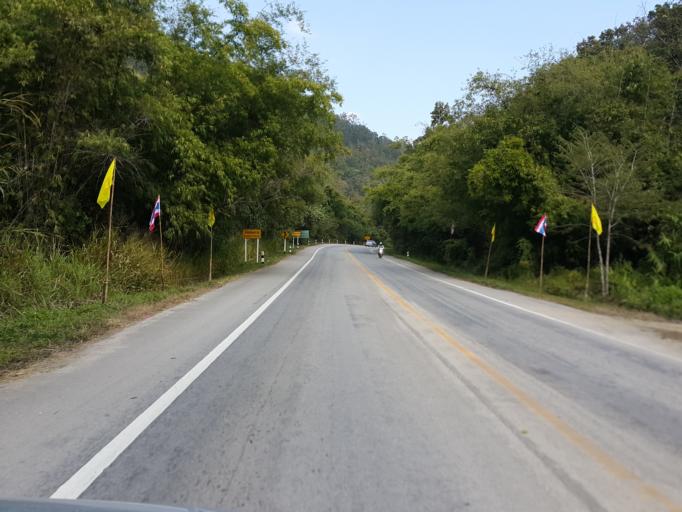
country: TH
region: Lampang
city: Wang Nuea
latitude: 19.0863
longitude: 99.4090
